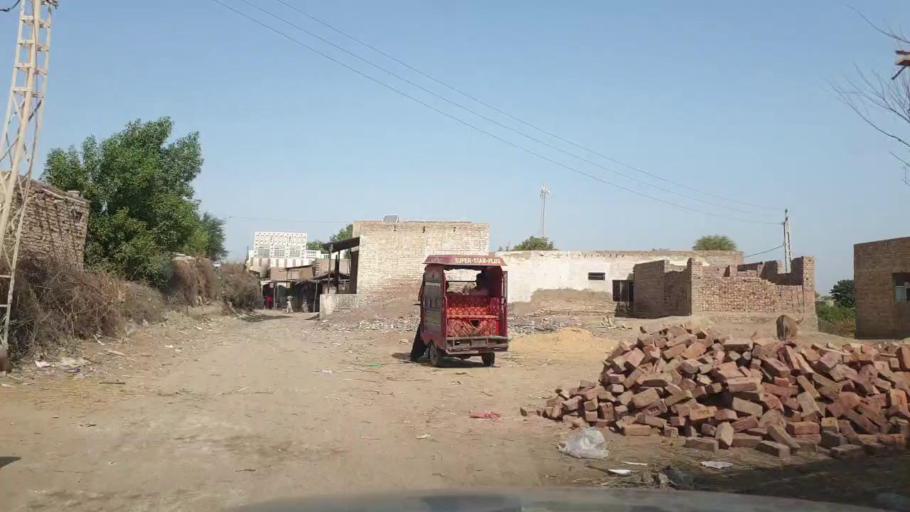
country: PK
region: Sindh
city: Tando Muhammad Khan
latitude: 25.1590
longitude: 68.3876
